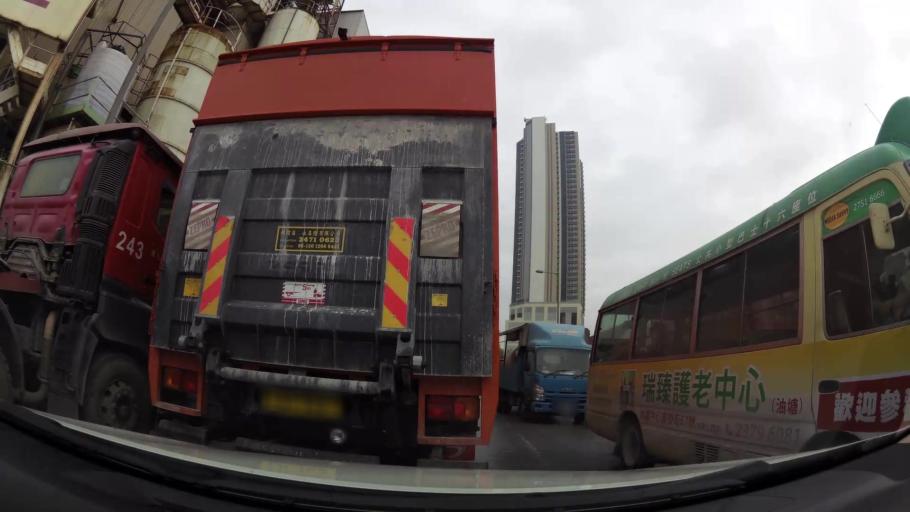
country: HK
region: Kowloon City
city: Kowloon
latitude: 22.2922
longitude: 114.2357
